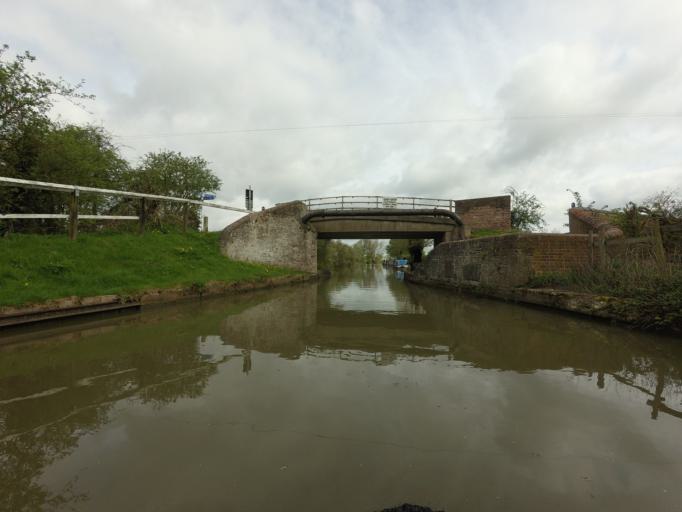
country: GB
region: England
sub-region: Milton Keynes
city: Water Eaton
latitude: 51.9554
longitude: -0.7079
